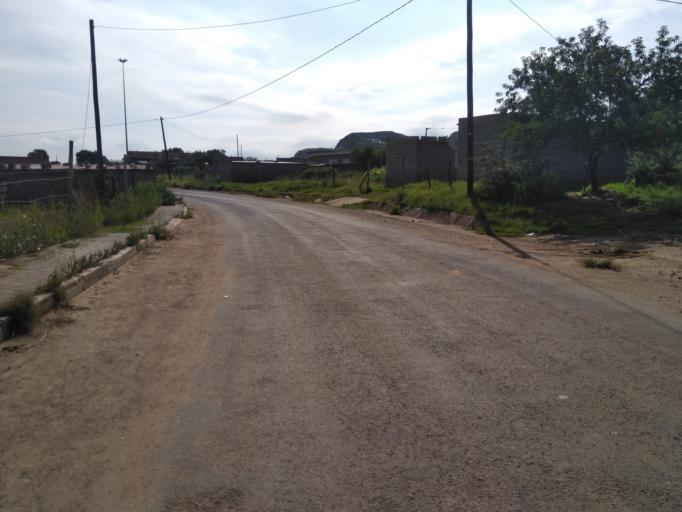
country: LS
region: Butha-Buthe
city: Butha-Buthe
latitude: -28.7739
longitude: 28.2491
